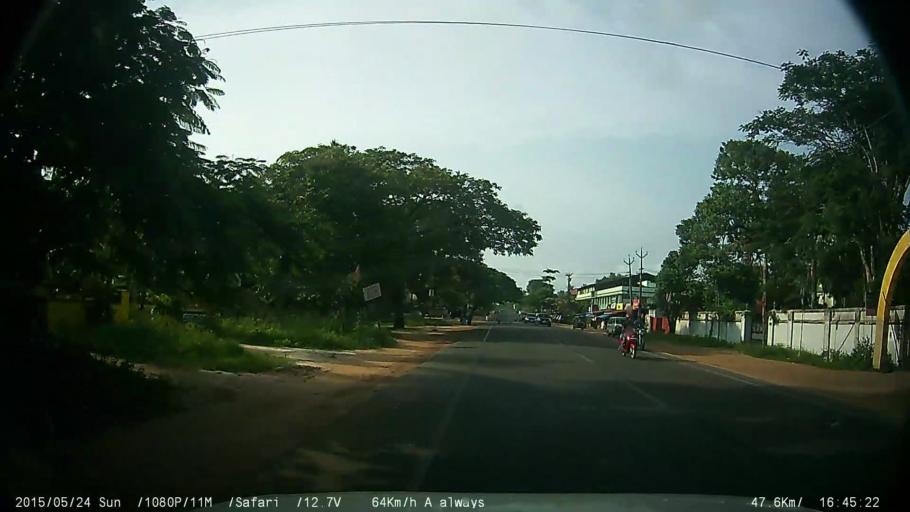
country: IN
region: Kerala
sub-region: Alappuzha
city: Shertallai
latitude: 9.6607
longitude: 76.3382
